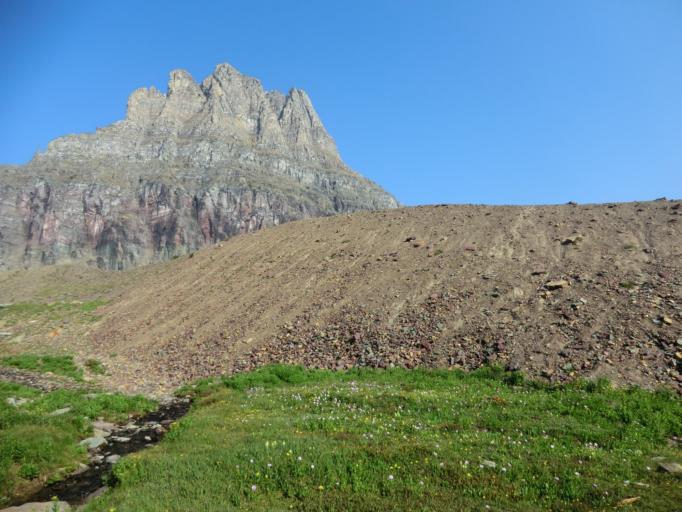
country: US
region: Montana
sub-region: Flathead County
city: Columbia Falls
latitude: 48.6894
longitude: -113.7331
